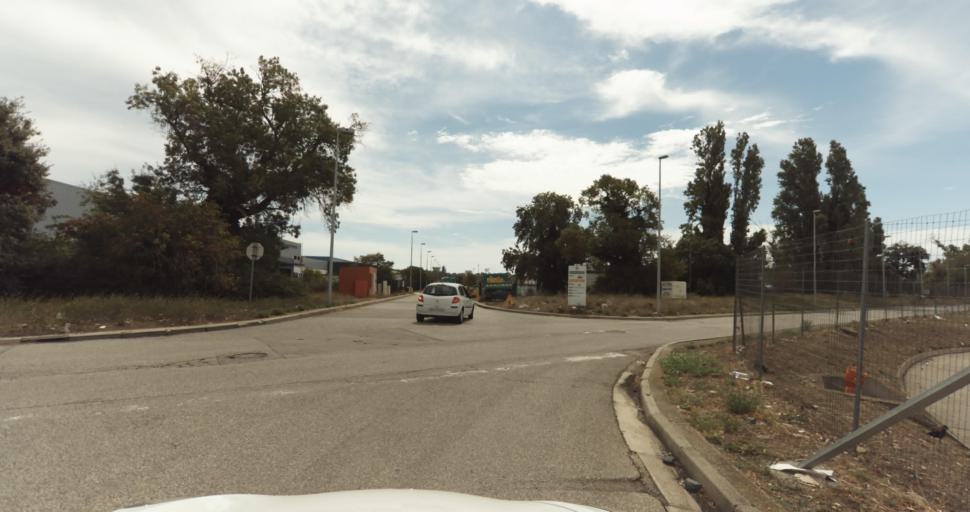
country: FR
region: Provence-Alpes-Cote d'Azur
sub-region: Departement des Bouches-du-Rhone
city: Miramas
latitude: 43.6068
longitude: 5.0001
